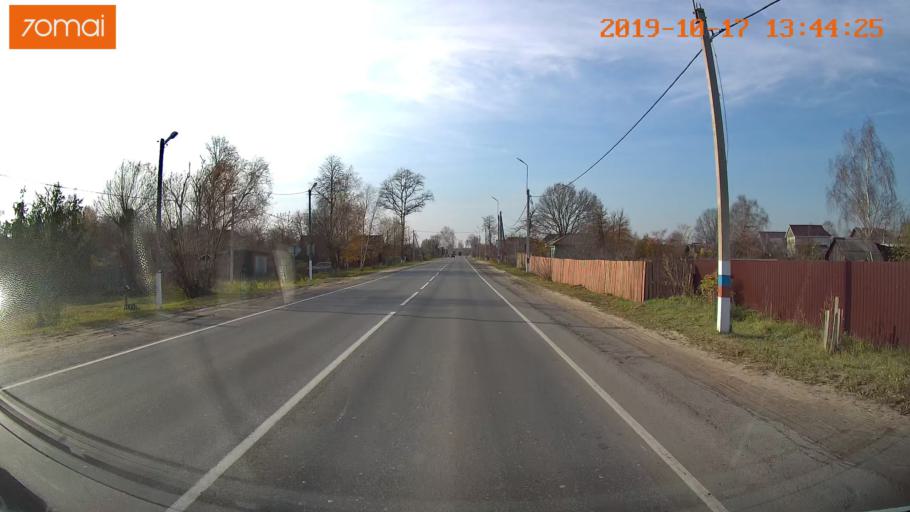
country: RU
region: Rjazan
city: Tuma
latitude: 55.1463
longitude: 40.5296
